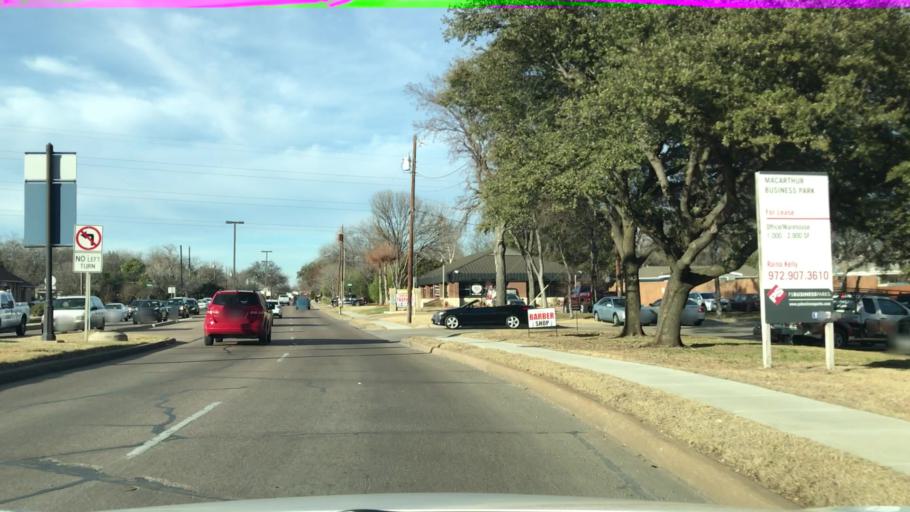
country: US
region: Texas
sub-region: Dallas County
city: Irving
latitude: 32.8155
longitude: -96.9597
